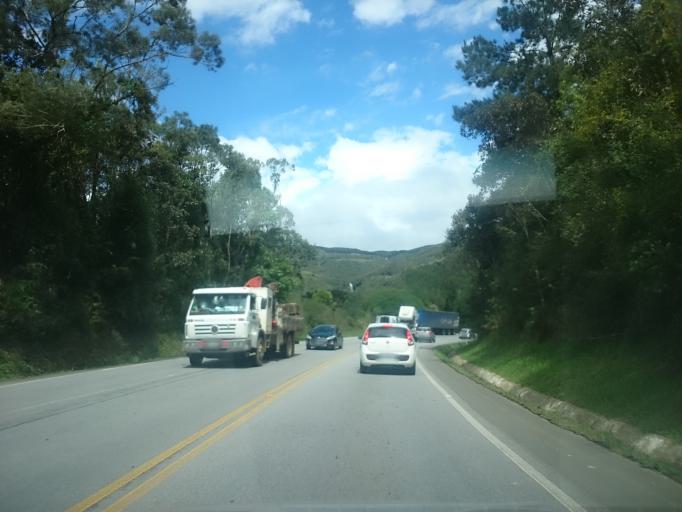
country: BR
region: Santa Catarina
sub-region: Anitapolis
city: Anitapolis
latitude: -27.6667
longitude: -49.2047
